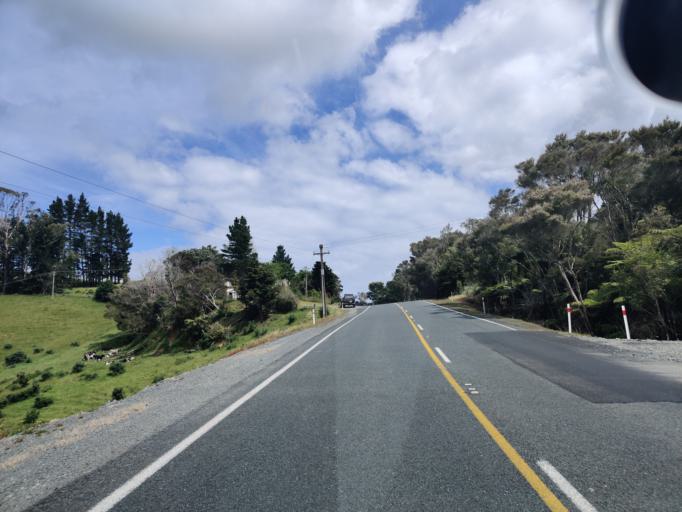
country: NZ
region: Northland
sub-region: Far North District
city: Taipa
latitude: -35.0618
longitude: 173.7086
